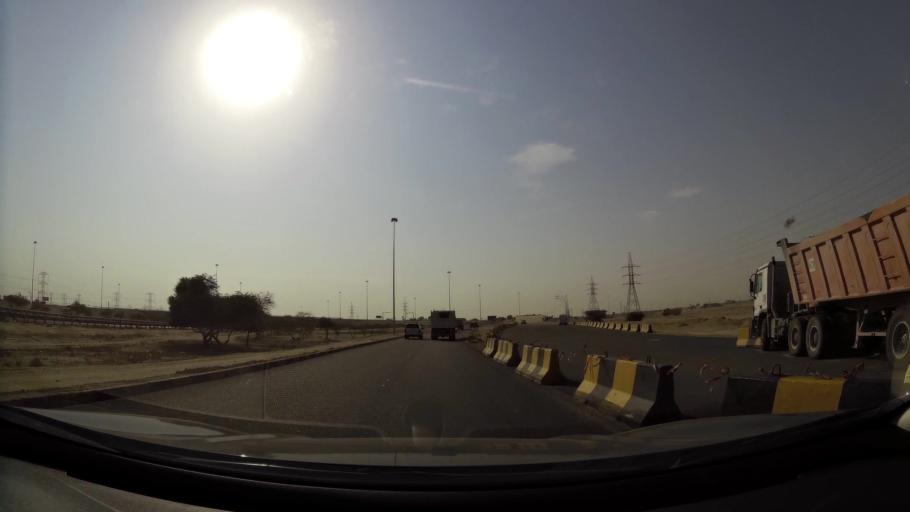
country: KW
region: Al Ahmadi
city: Al Ahmadi
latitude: 28.9612
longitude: 48.1200
